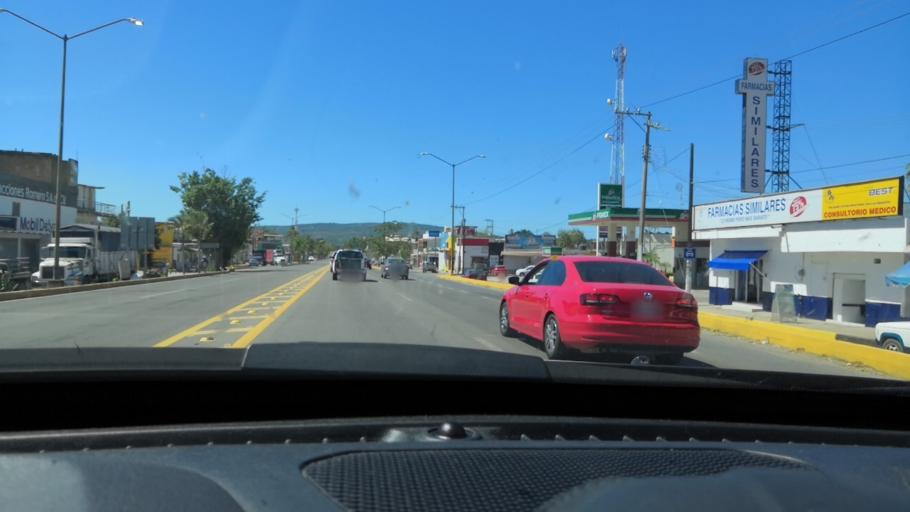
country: MX
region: Nayarit
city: Las Varas
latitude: 21.1794
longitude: -105.1367
